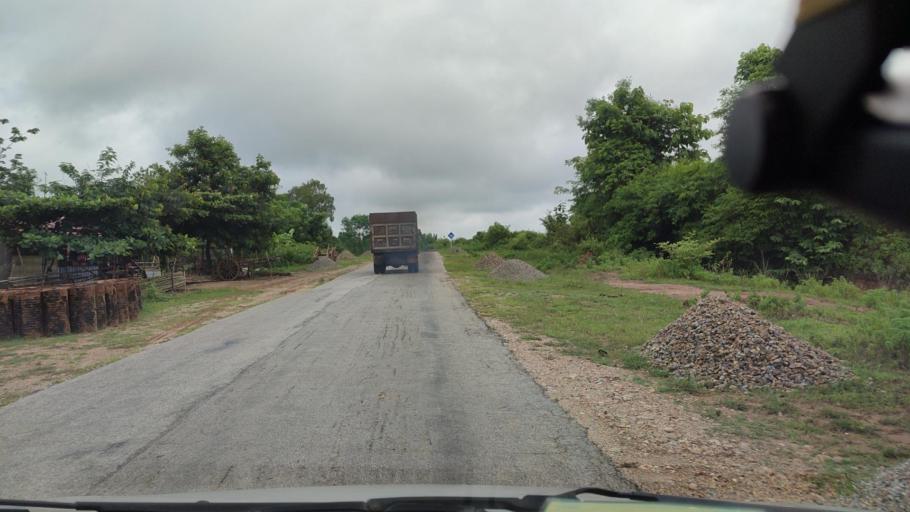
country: MM
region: Mandalay
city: Nay Pyi Taw
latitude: 19.9746
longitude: 95.9796
